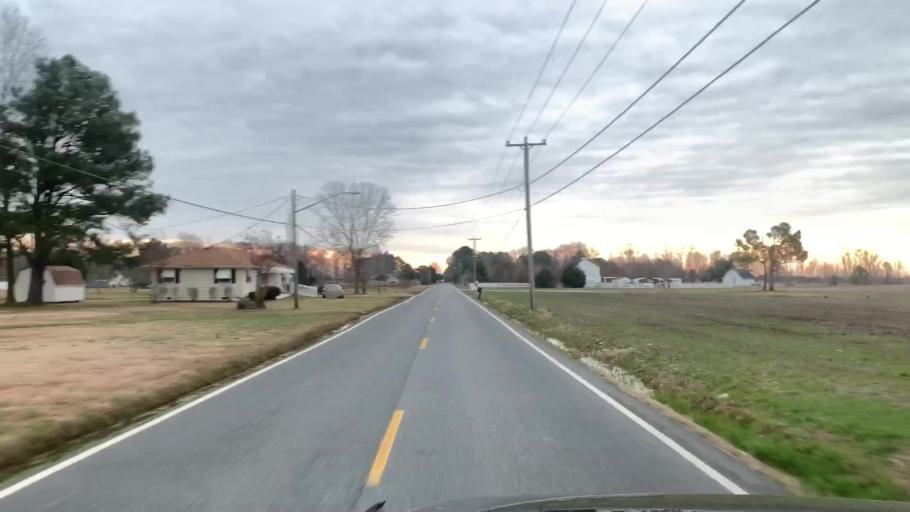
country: US
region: North Carolina
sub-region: Currituck County
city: Moyock
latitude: 36.6265
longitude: -76.1650
